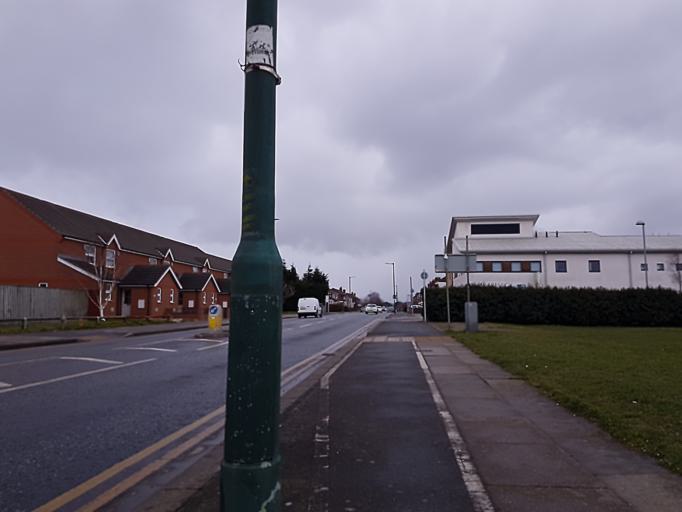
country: GB
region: England
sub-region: North East Lincolnshire
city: Grimbsy
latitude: 53.5684
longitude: -0.1101
